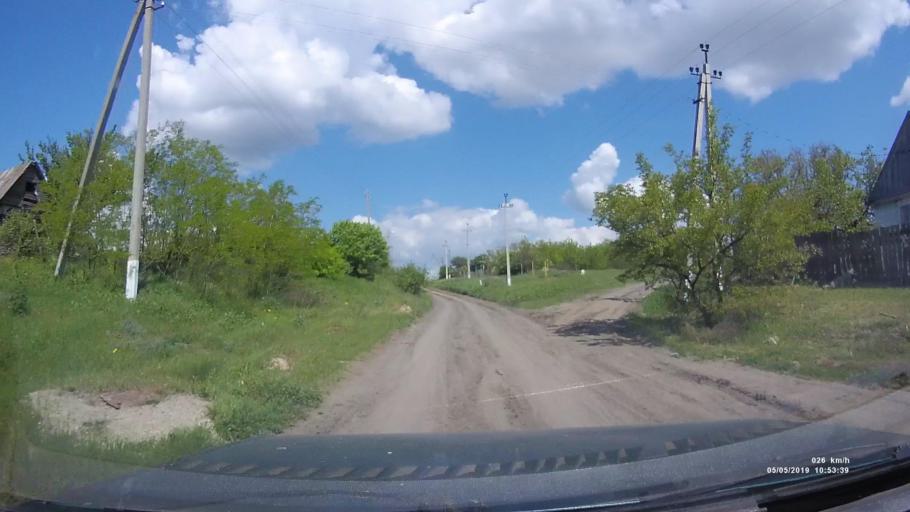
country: RU
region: Rostov
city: Ust'-Donetskiy
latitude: 47.6548
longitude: 40.8243
